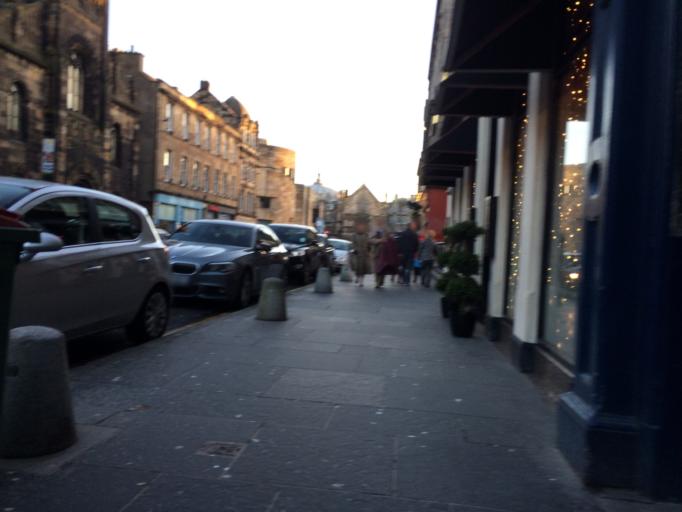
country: GB
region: Scotland
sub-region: Edinburgh
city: Edinburgh
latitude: 55.9479
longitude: -3.1918
